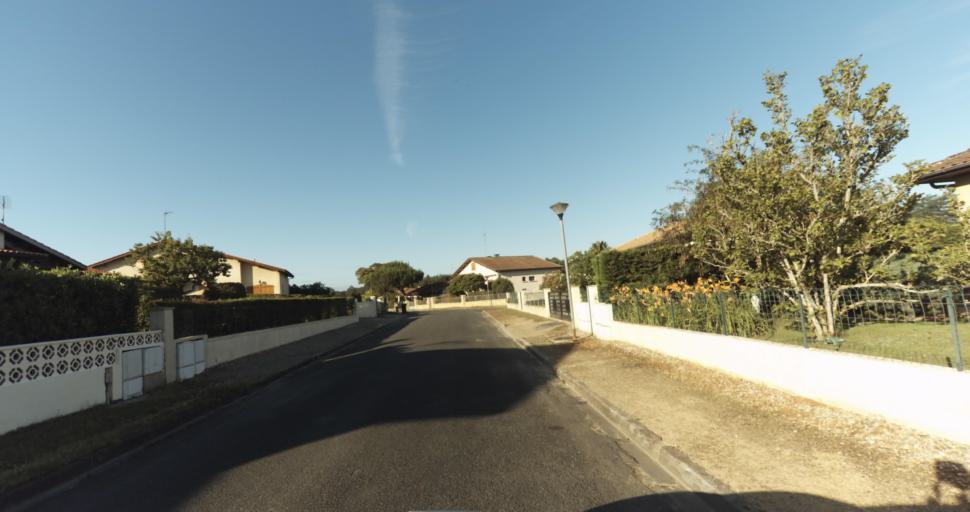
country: FR
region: Aquitaine
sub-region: Departement de la Gironde
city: Bazas
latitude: 44.4247
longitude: -0.2191
